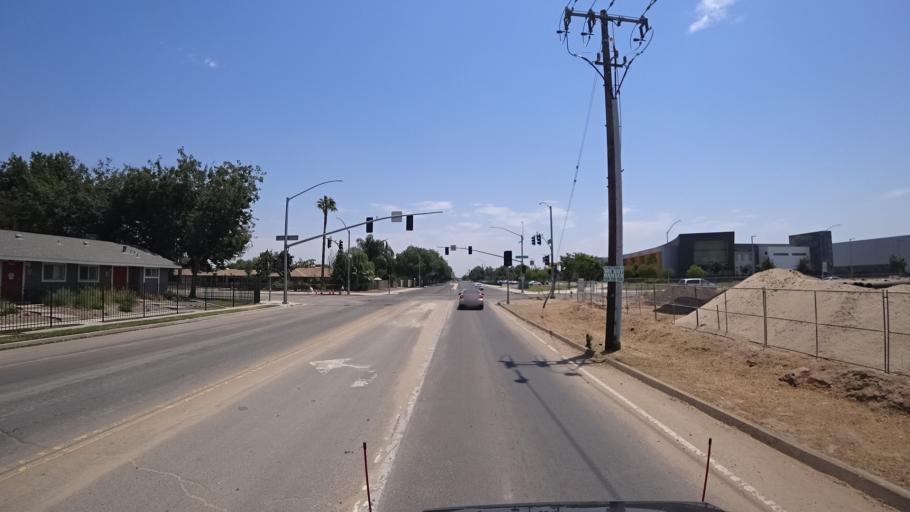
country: US
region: California
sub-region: Fresno County
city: Fresno
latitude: 36.7141
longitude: -119.8003
